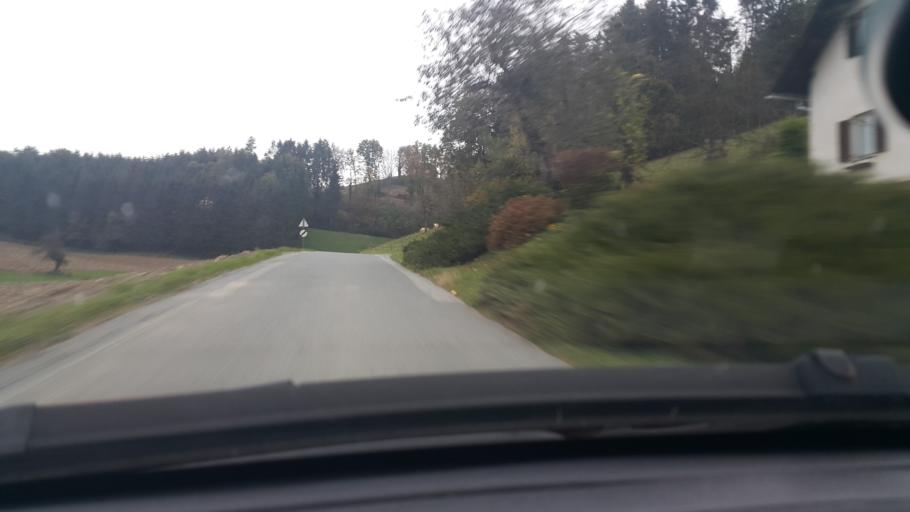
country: AT
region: Styria
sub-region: Politischer Bezirk Deutschlandsberg
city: Wies
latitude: 46.7164
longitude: 15.3051
